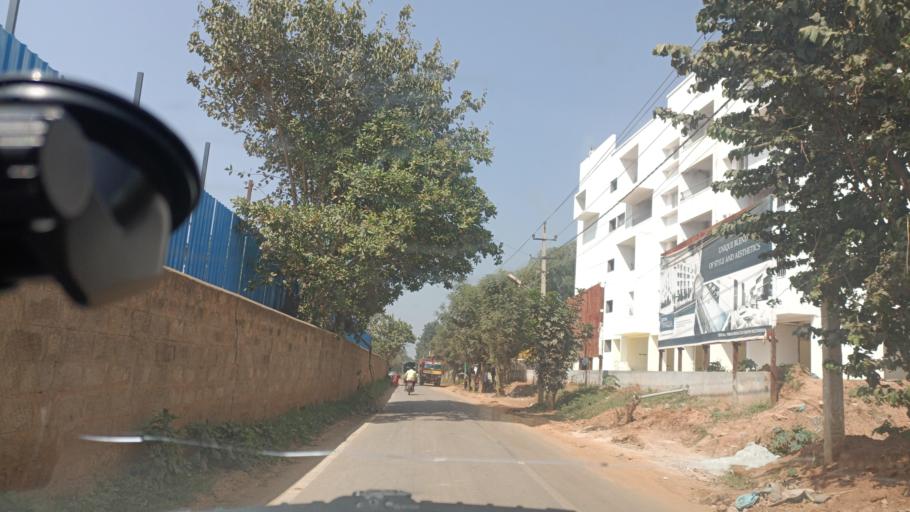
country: IN
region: Karnataka
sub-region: Bangalore Urban
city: Yelahanka
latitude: 13.1200
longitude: 77.6082
